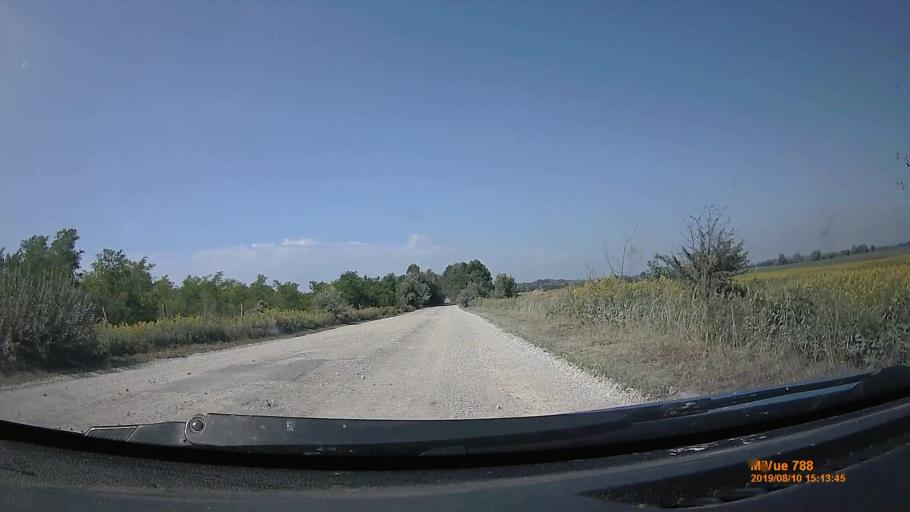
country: HU
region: Somogy
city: Fonyod
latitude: 46.6935
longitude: 17.5600
